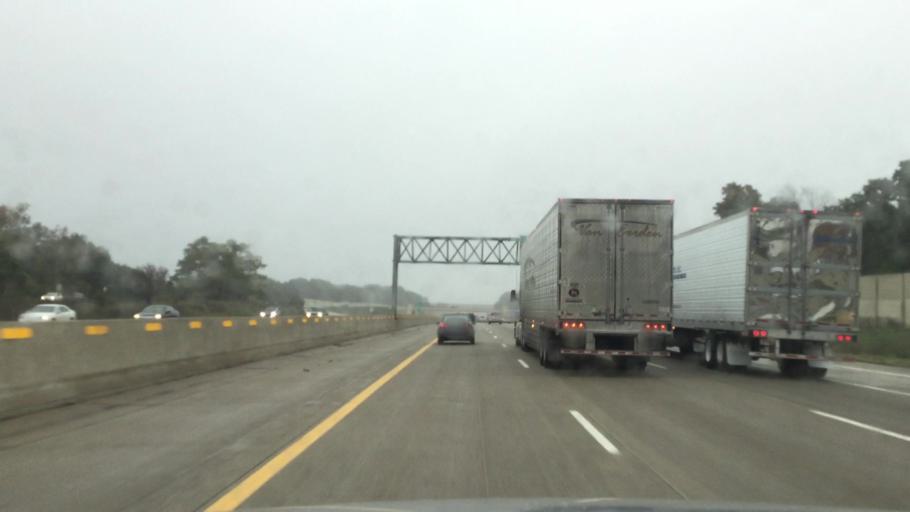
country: US
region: Michigan
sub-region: Kalamazoo County
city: Portage
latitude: 42.2379
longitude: -85.6202
